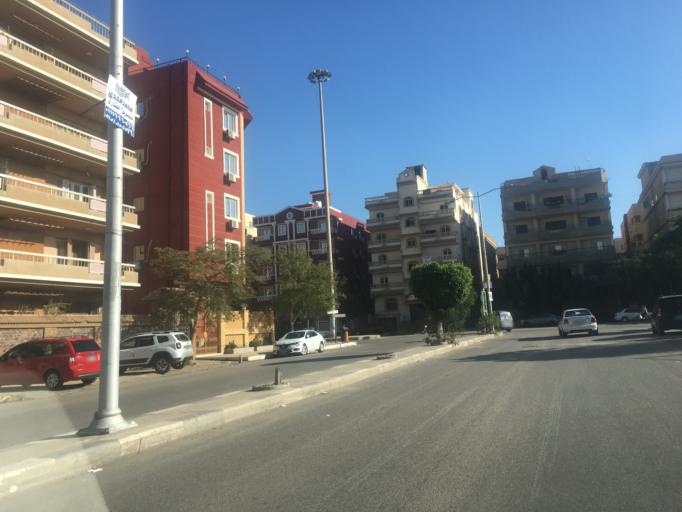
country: EG
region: Al Jizah
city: Madinat Sittah Uktubar
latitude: 29.9811
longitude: 30.9461
